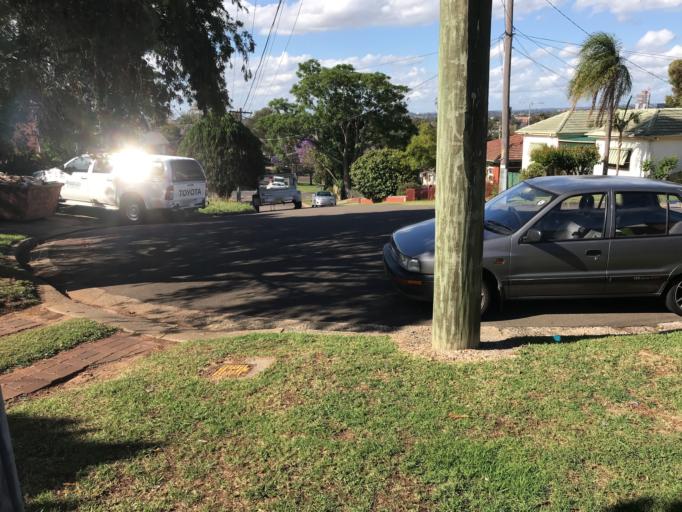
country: AU
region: New South Wales
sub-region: Blacktown
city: Blacktown
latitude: -33.7789
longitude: 150.8936
